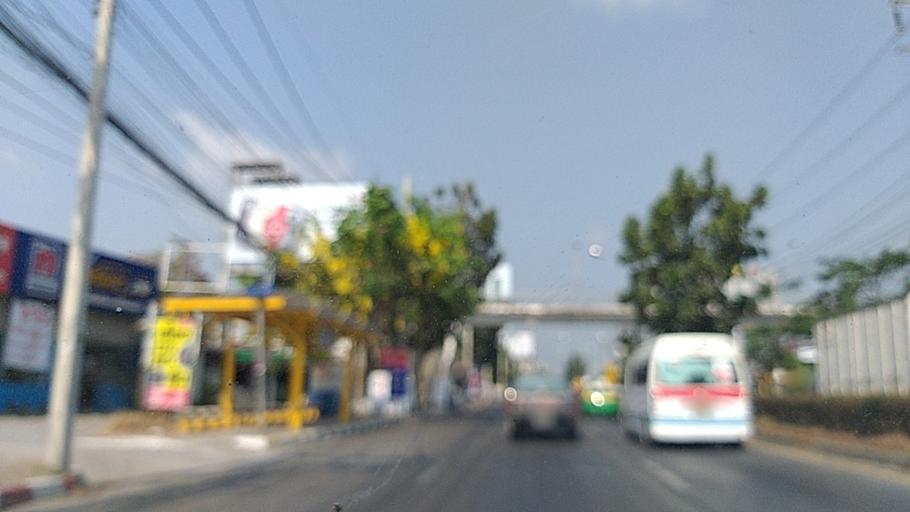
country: TH
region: Bangkok
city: Sai Mai
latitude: 13.9319
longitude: 100.6646
